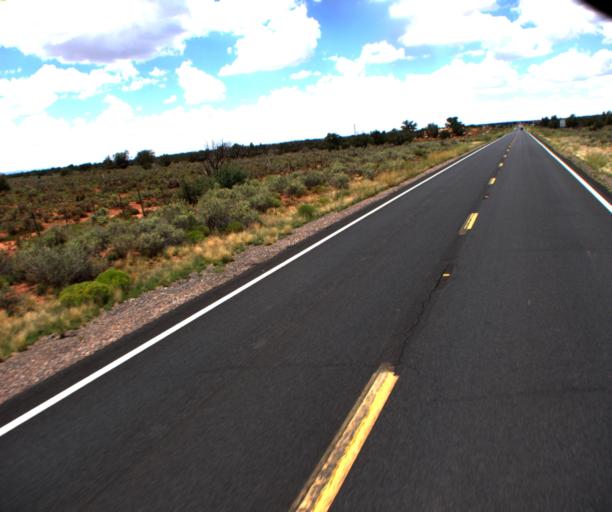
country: US
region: Arizona
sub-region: Coconino County
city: Williams
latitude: 35.6374
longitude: -112.1239
